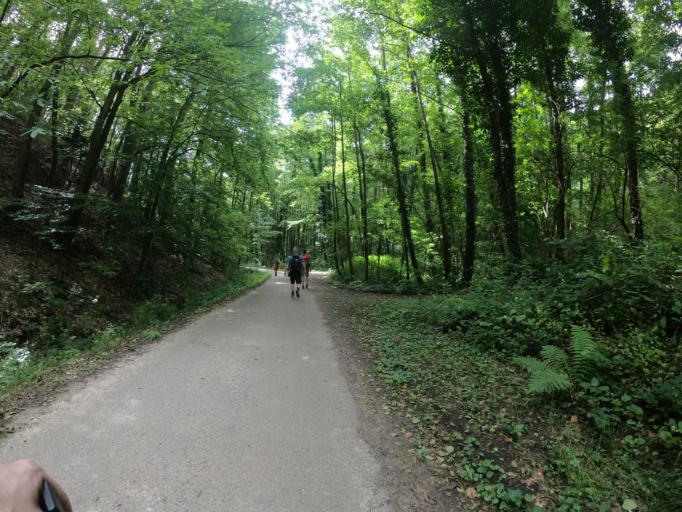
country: DE
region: Rheinland-Pfalz
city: Bad Bergzabern
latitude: 49.1145
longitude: 7.9906
